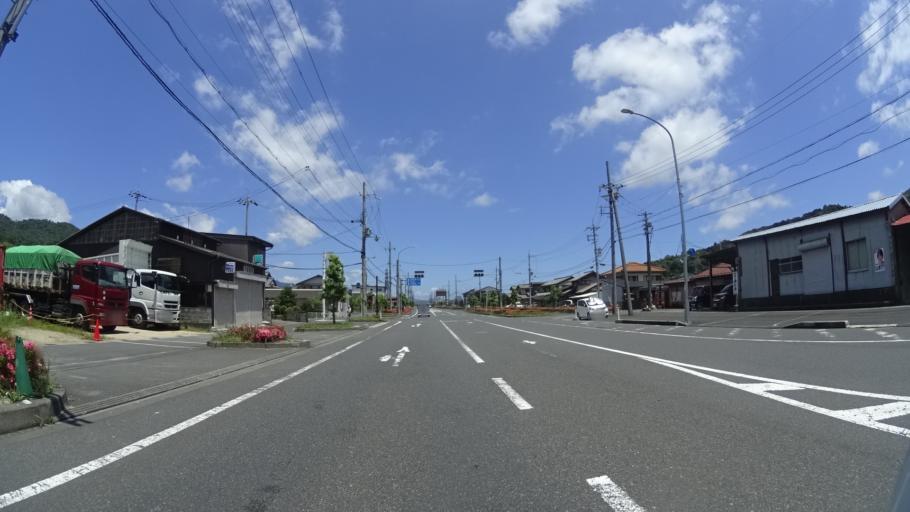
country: JP
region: Kyoto
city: Miyazu
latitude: 35.5212
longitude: 135.1894
